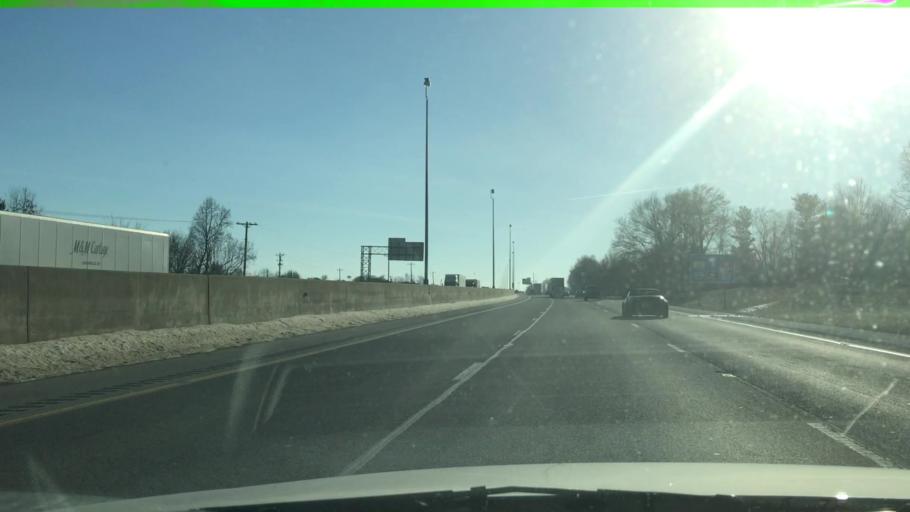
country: US
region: Kentucky
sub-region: Warren County
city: Bowling Green
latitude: 36.9494
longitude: -86.4094
